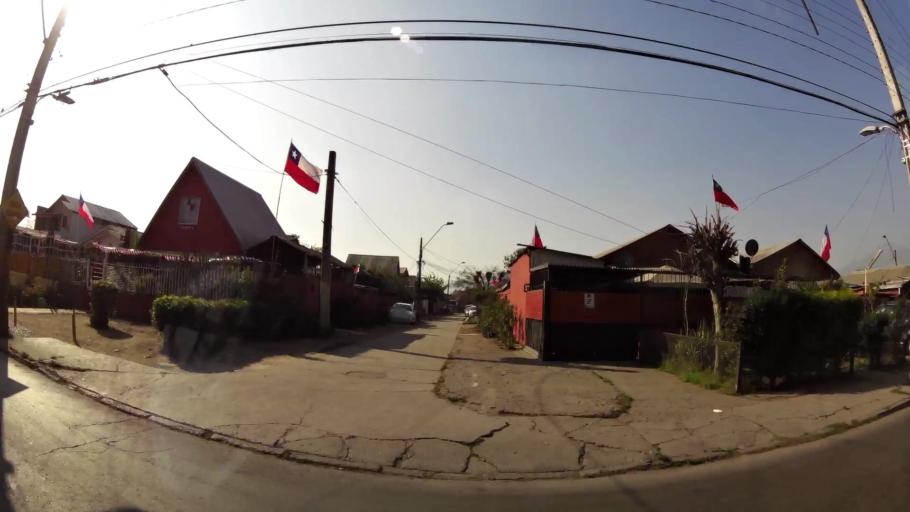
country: CL
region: Santiago Metropolitan
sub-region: Provincia de Santiago
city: Lo Prado
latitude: -33.3741
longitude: -70.6907
